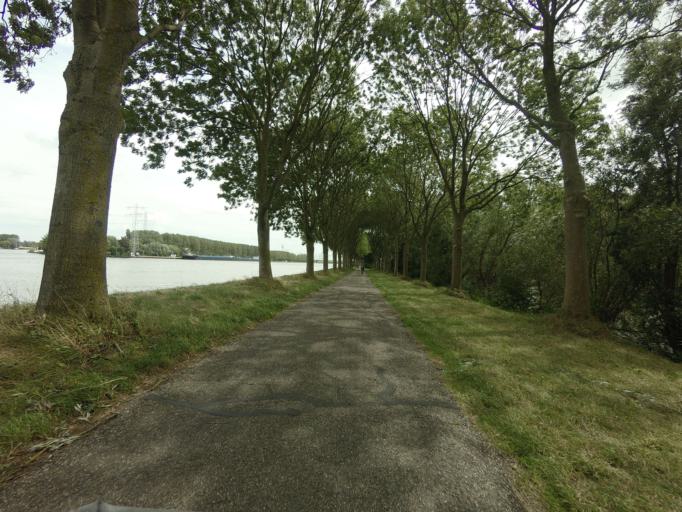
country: NL
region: North Holland
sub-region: Gemeente Diemen
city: Diemen
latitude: 52.3414
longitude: 4.9986
